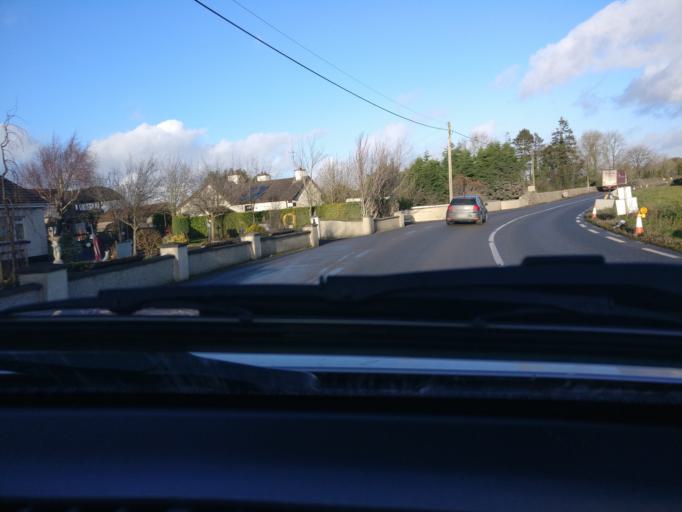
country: IE
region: Leinster
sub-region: An Iarmhi
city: Rathwire
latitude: 53.5784
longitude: -7.1558
